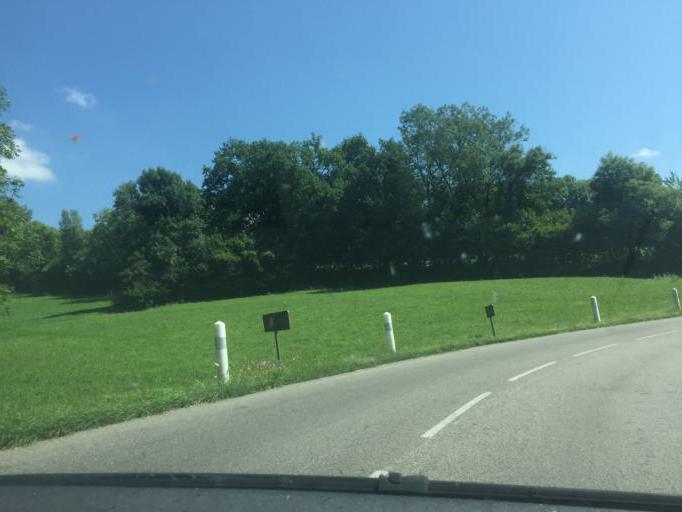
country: FR
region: Rhone-Alpes
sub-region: Departement de la Haute-Savoie
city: Lovagny
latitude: 45.9202
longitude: 6.0129
